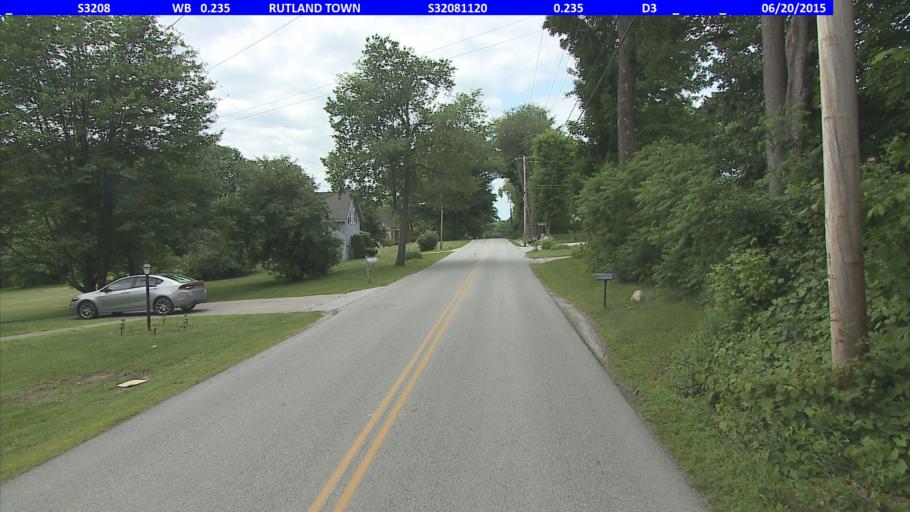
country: US
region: Vermont
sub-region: Rutland County
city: Rutland
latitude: 43.6086
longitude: -72.9407
